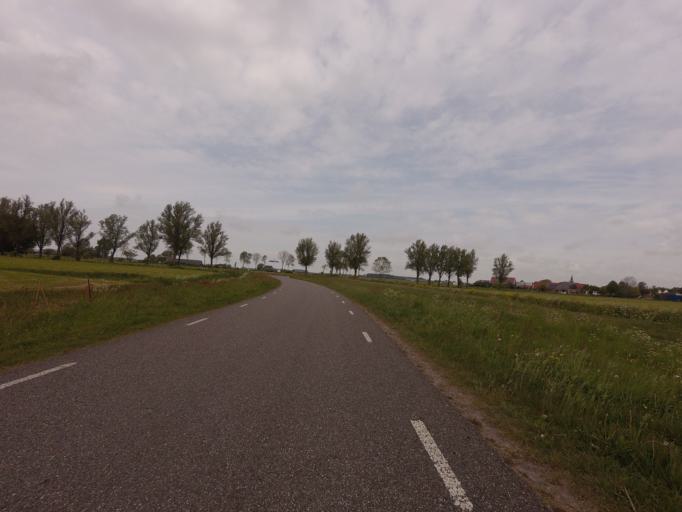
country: NL
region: Friesland
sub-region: Sudwest Fryslan
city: Bolsward
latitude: 53.0783
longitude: 5.4807
